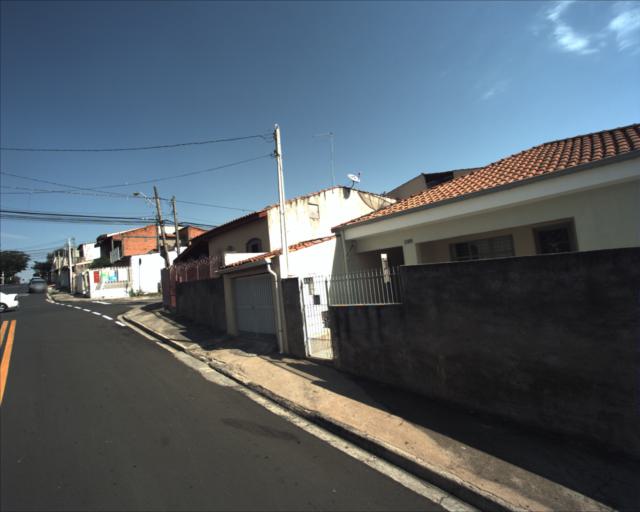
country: BR
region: Sao Paulo
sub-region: Sorocaba
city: Sorocaba
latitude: -23.4758
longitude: -47.4673
